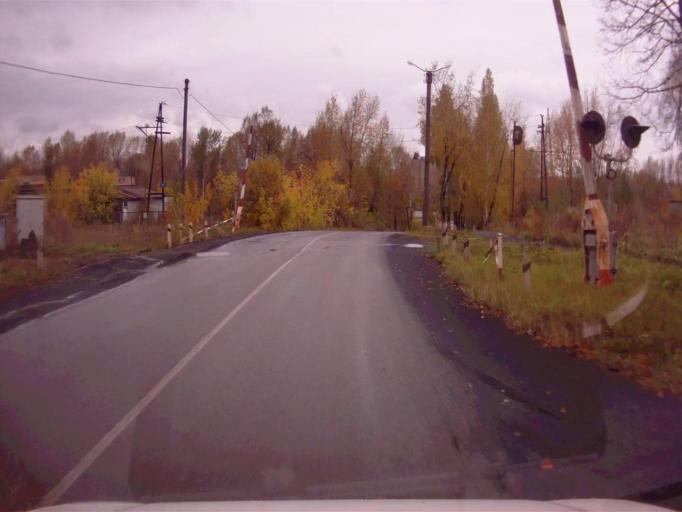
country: RU
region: Chelyabinsk
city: Verkhniy Ufaley
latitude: 56.0420
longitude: 60.2501
